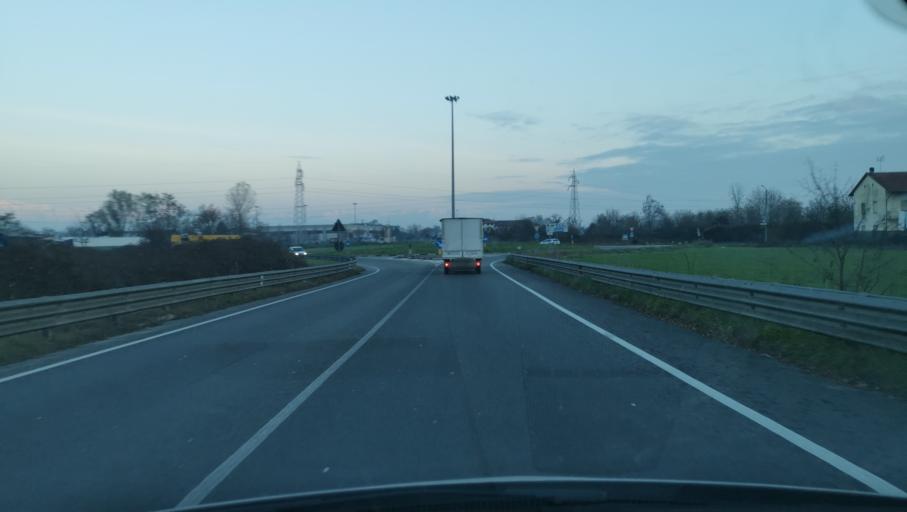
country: IT
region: Piedmont
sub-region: Provincia di Torino
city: Chivasso
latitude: 45.2118
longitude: 7.8902
